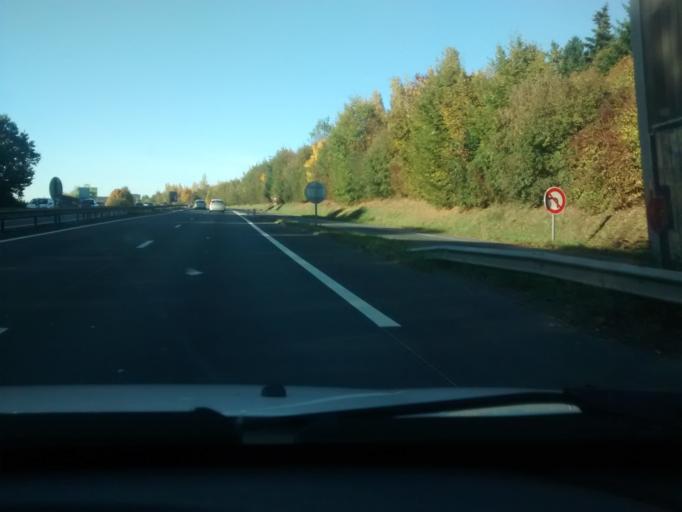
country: FR
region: Brittany
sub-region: Departement d'Ille-et-Vilaine
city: Saint-Jacques-de-la-Lande
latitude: 48.0842
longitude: -1.6987
